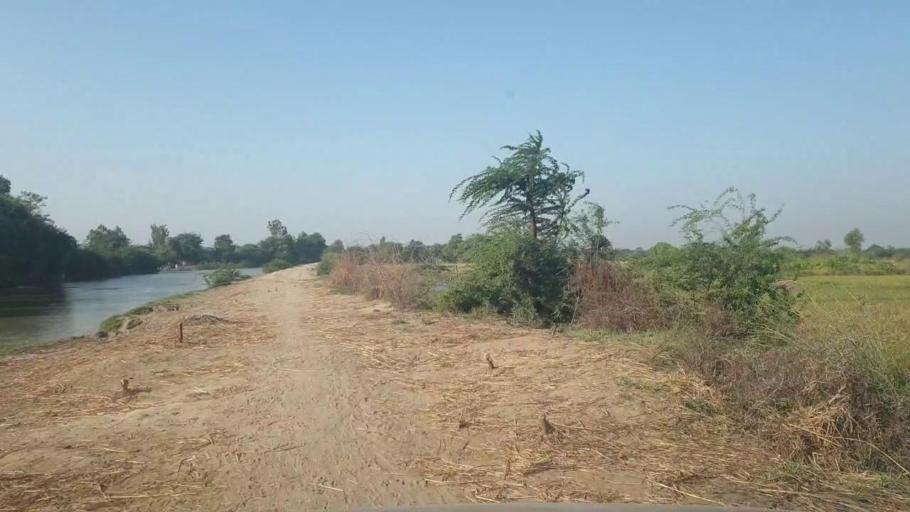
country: PK
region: Sindh
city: Tando Bago
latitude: 24.7154
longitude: 68.9110
